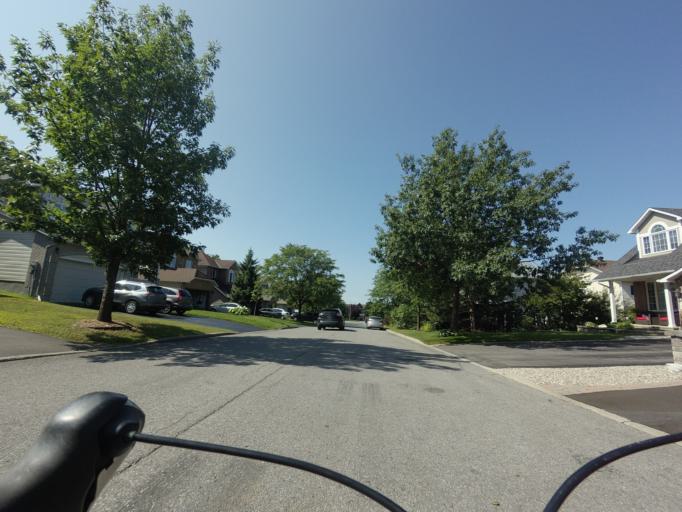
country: CA
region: Ontario
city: Bells Corners
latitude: 45.2796
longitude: -75.8417
